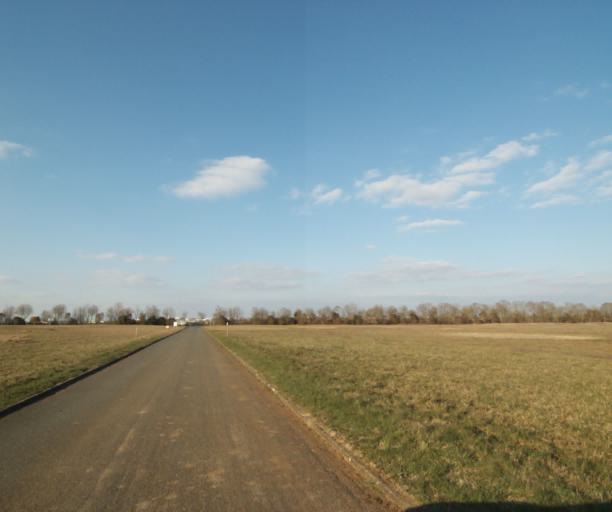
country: FR
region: Poitou-Charentes
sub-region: Departement des Deux-Sevres
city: Aiffres
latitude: 46.3164
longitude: -0.3993
